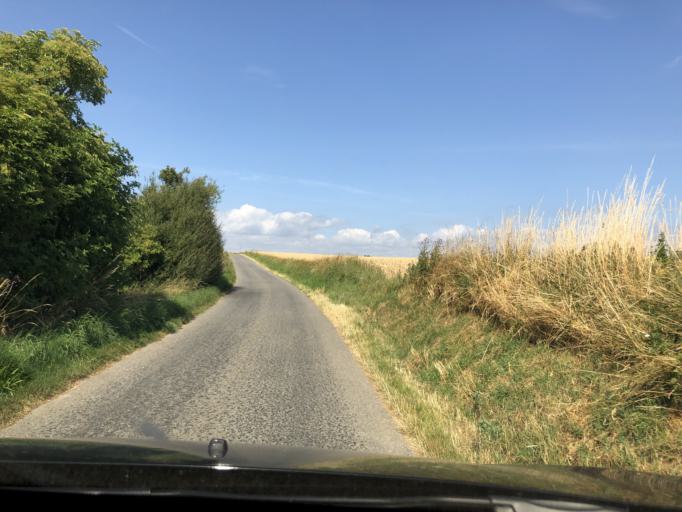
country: DK
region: South Denmark
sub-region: AEro Kommune
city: AEroskobing
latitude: 54.9067
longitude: 10.2769
